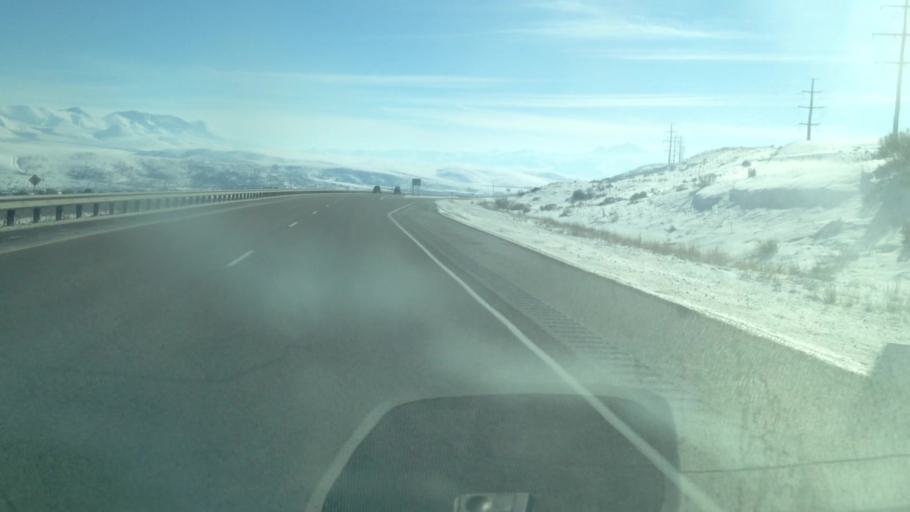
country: US
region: Idaho
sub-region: Oneida County
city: Malad City
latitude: 42.3097
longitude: -112.2117
